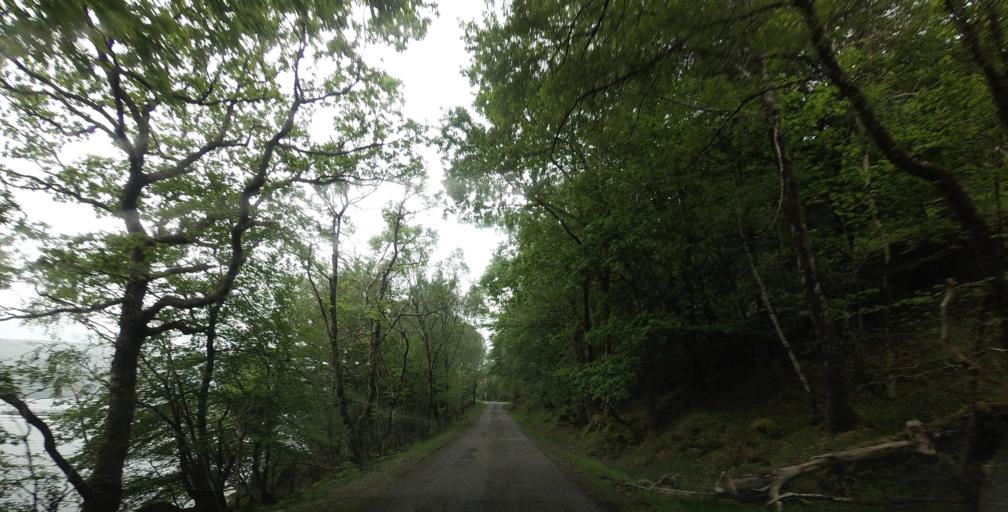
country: GB
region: Scotland
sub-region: Highland
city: Fort William
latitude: 56.7920
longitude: -5.1734
